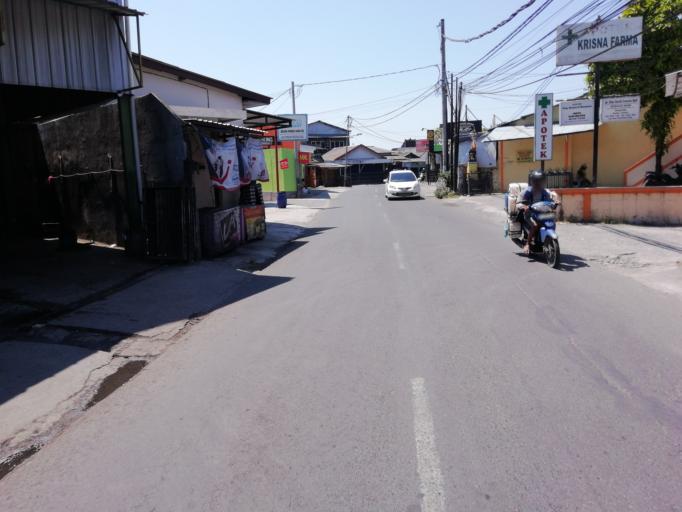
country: ID
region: Bali
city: Karyadharma
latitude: -8.6934
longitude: 115.1927
